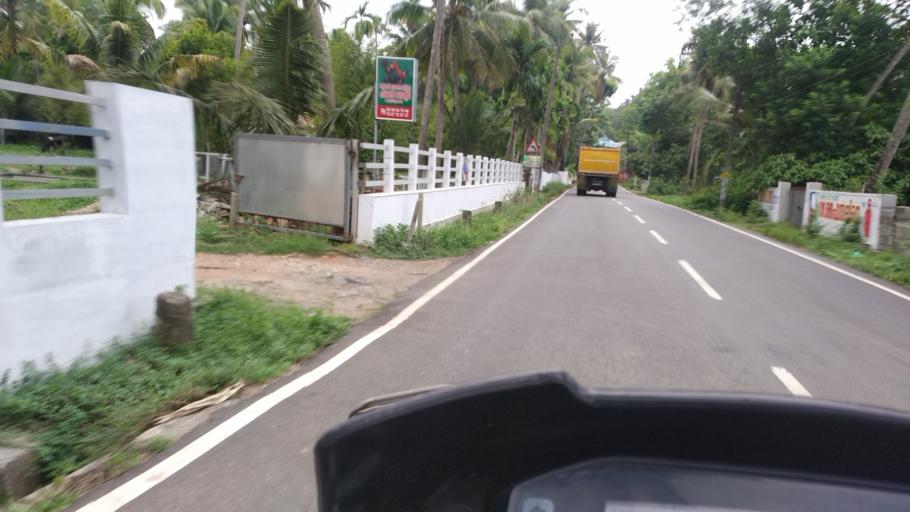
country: IN
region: Kerala
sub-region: Ernakulam
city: Aluva
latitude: 10.1543
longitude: 76.2904
